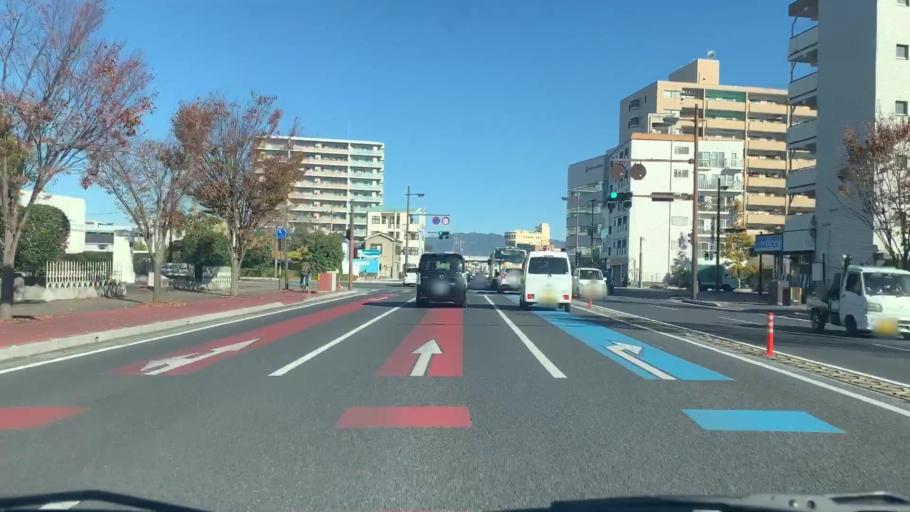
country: JP
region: Saga Prefecture
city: Saga-shi
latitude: 33.2607
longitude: 130.2932
